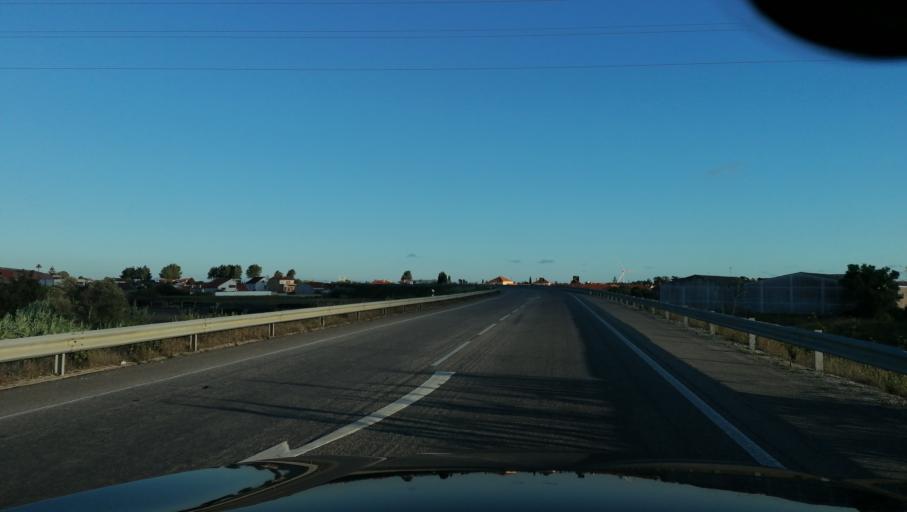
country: PT
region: Aveiro
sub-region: Aveiro
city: Oliveirinha
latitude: 40.5945
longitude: -8.6121
